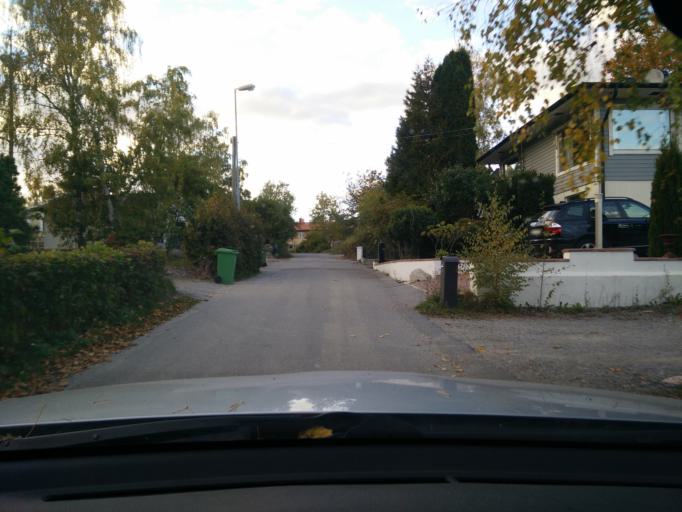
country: SE
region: Stockholm
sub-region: Stockholms Kommun
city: Kista
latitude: 59.4150
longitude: 17.9440
